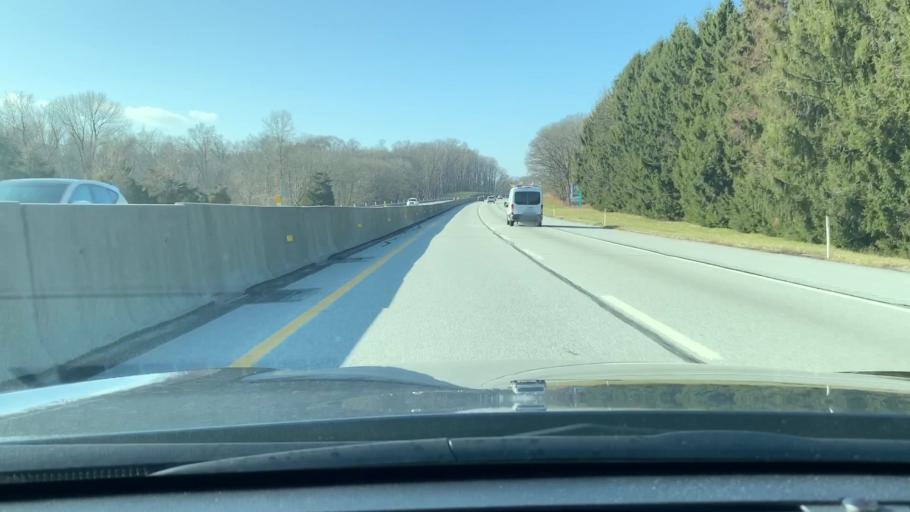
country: US
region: Pennsylvania
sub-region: Lancaster County
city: Elizabethtown
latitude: 40.2071
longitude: -76.6409
